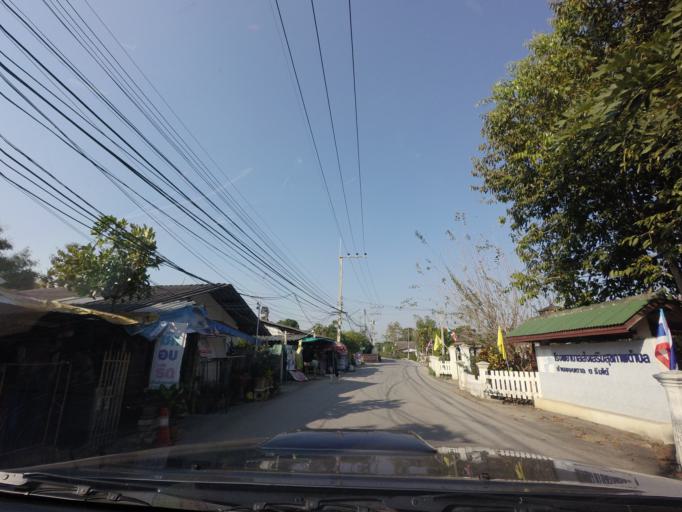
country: TH
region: Chiang Mai
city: San Sai
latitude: 18.9186
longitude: 98.9659
